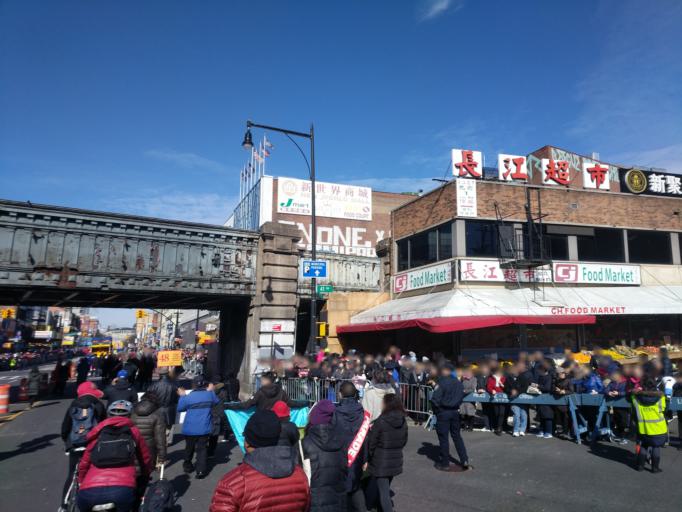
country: US
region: New York
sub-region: Queens County
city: Jamaica
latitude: 40.7585
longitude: -73.8295
